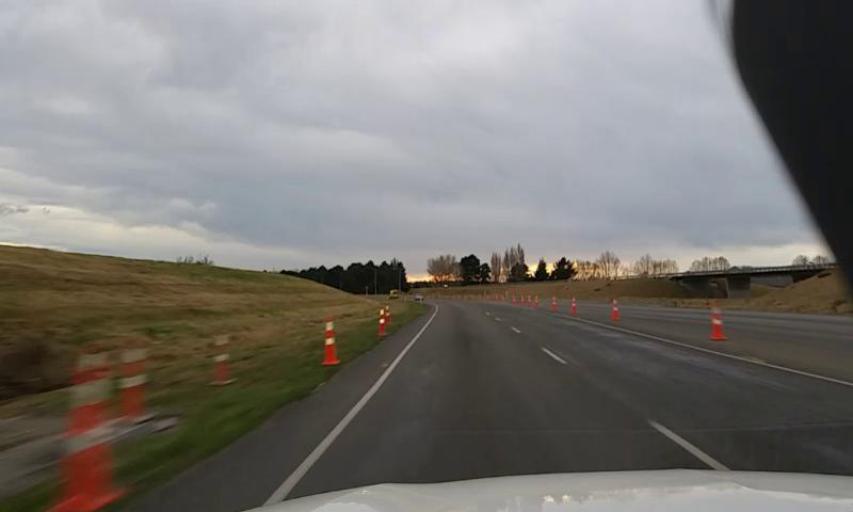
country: NZ
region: Canterbury
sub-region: Waimakariri District
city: Kaiapoi
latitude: -43.4304
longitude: 172.6439
